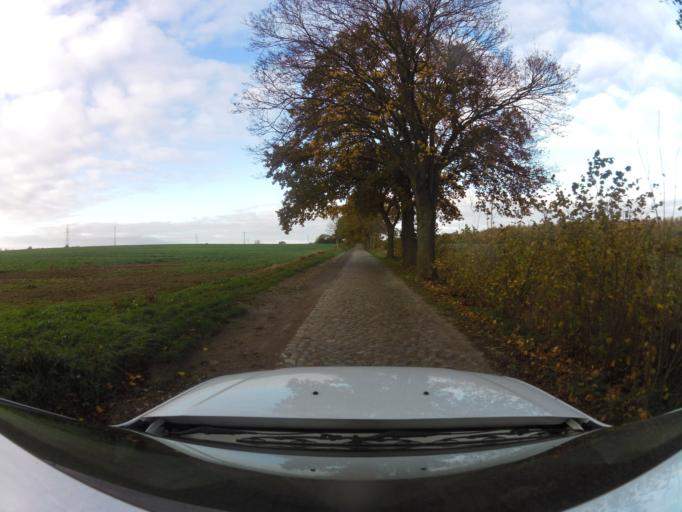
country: PL
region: West Pomeranian Voivodeship
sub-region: Powiat gryficki
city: Trzebiatow
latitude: 54.0442
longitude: 15.2279
